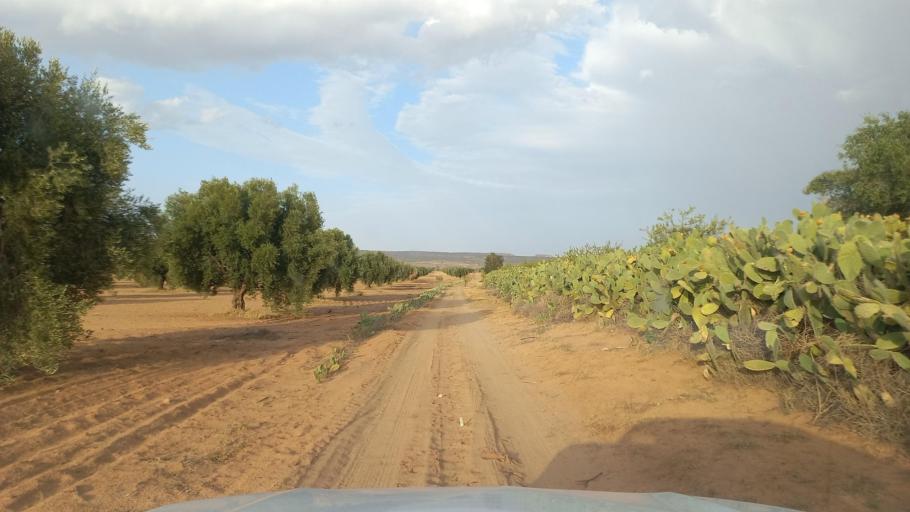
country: TN
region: Al Qasrayn
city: Sbiba
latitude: 35.2863
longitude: 9.0763
